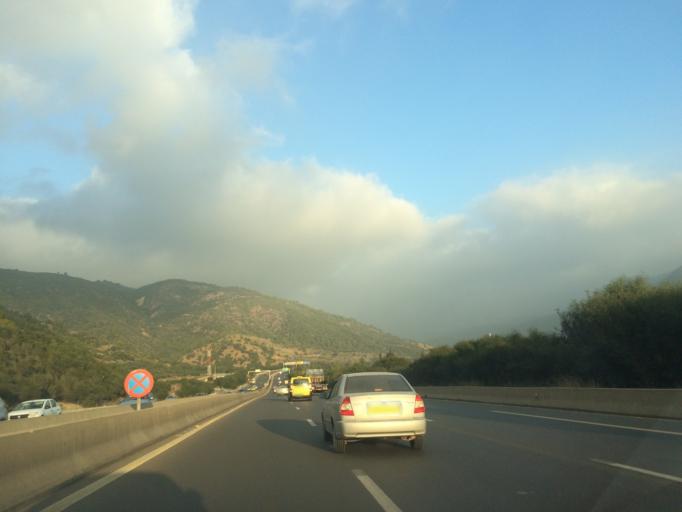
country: DZ
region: Tipaza
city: Hadjout
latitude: 36.3896
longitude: 2.4987
